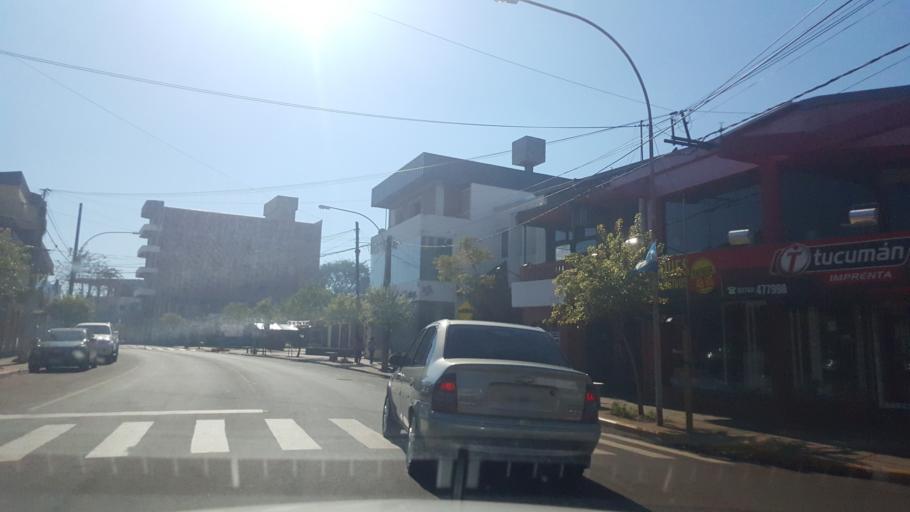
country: AR
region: Misiones
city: Puerto Rico
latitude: -26.8133
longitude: -55.0254
